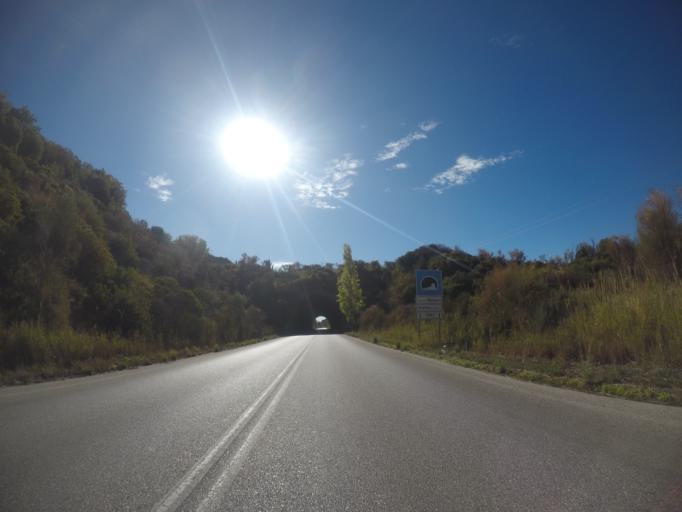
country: GR
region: Epirus
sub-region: Nomos Prevezis
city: Kanalaki
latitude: 39.1666
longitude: 20.5599
